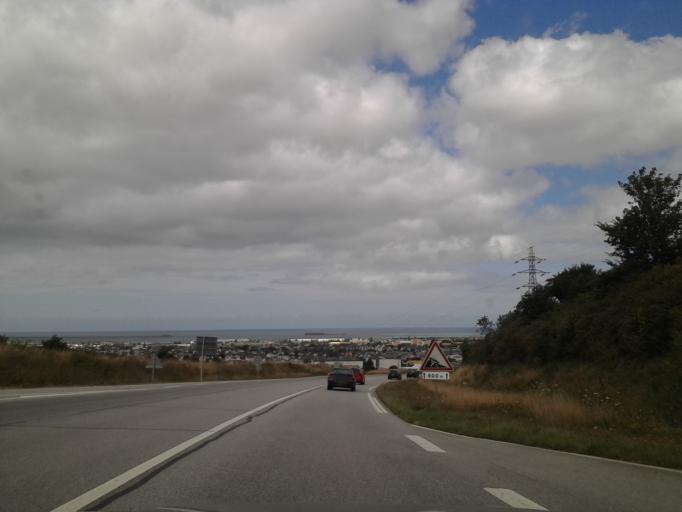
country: FR
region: Lower Normandy
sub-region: Departement de la Manche
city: Tourlaville
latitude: 49.6270
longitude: -1.5819
